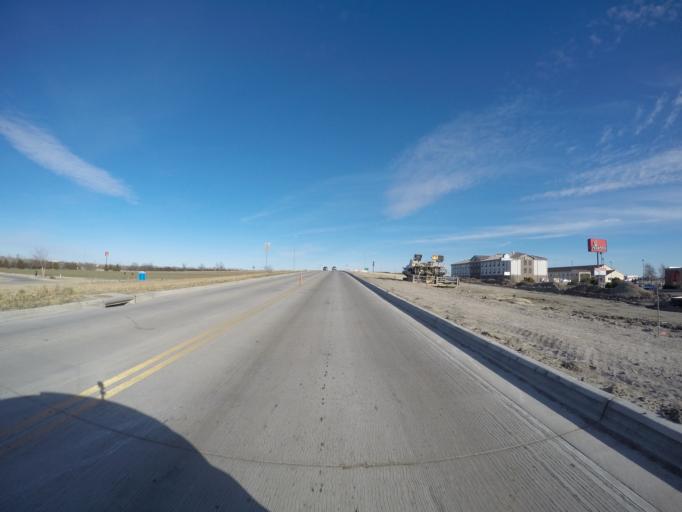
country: US
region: Kansas
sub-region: McPherson County
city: McPherson
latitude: 38.3710
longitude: -97.6244
